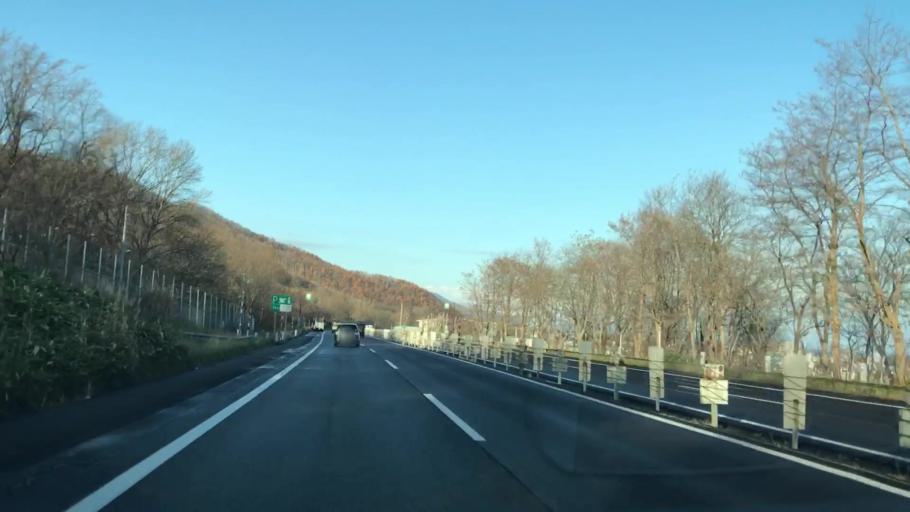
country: JP
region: Hokkaido
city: Sapporo
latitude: 43.1184
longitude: 141.2271
